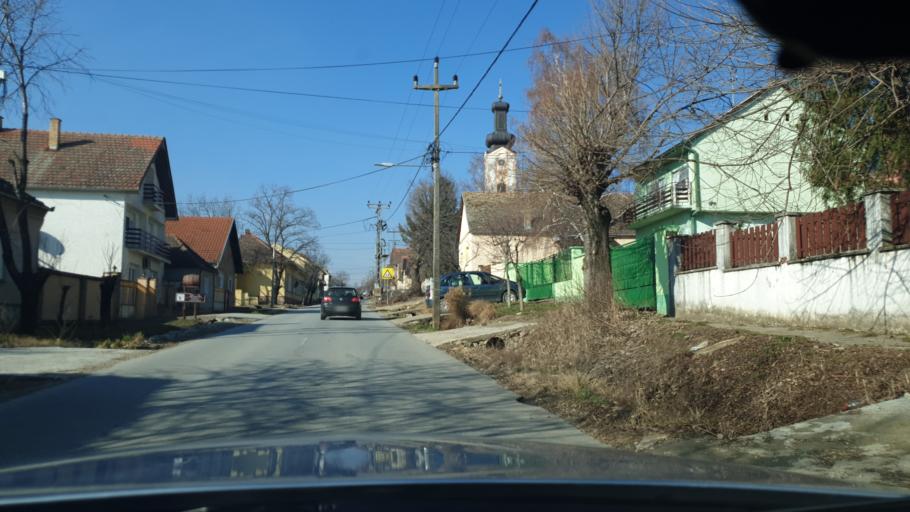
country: RS
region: Autonomna Pokrajina Vojvodina
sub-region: Sremski Okrug
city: Irig
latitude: 45.0882
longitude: 19.8355
